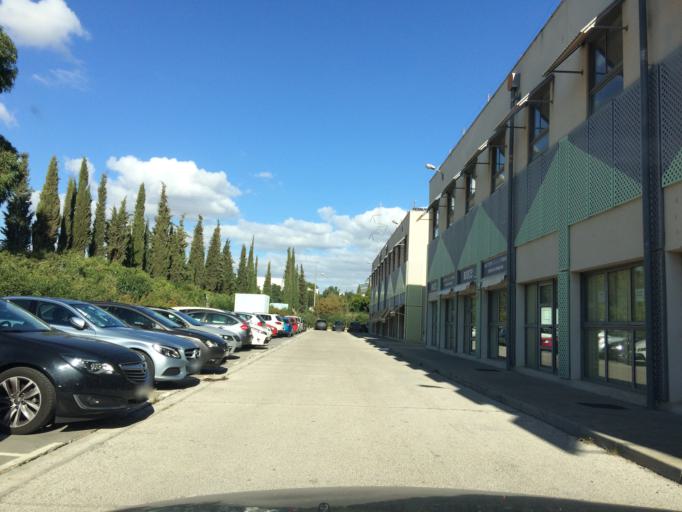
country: ES
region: Andalusia
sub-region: Provincia de Malaga
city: Alhaurin de la Torre
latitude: 36.7313
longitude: -4.5480
